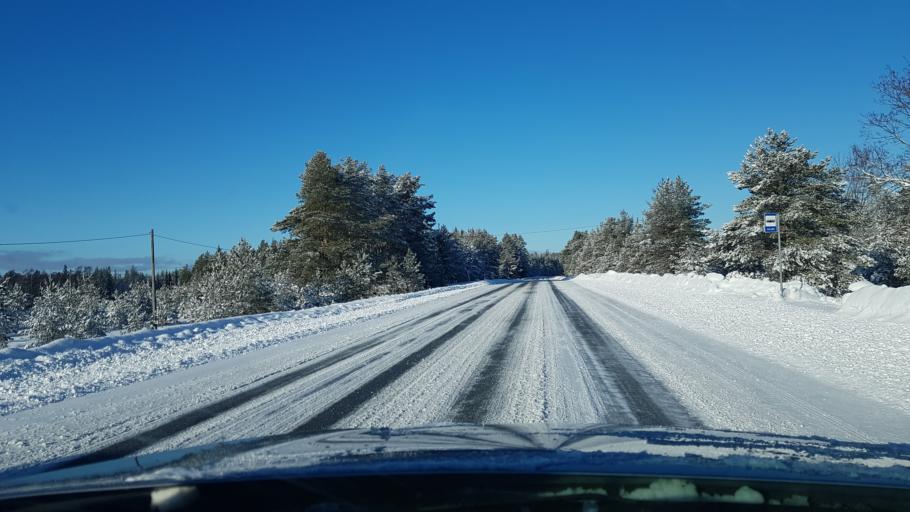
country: EE
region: Hiiumaa
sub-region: Kaerdla linn
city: Kardla
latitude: 58.9437
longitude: 22.7743
